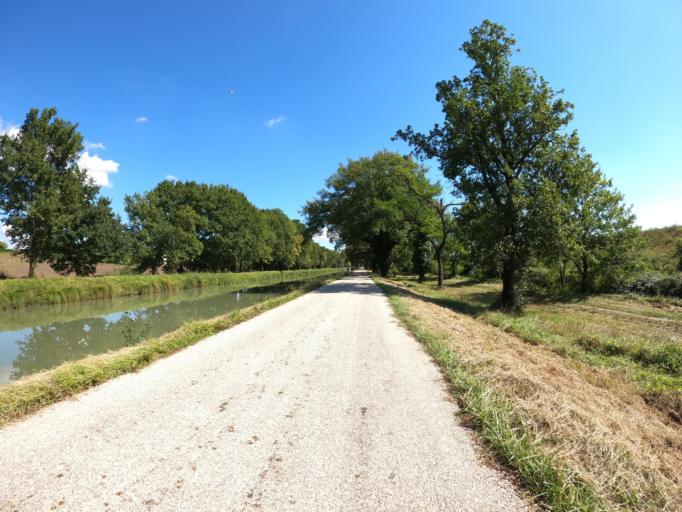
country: FR
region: Midi-Pyrenees
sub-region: Departement du Tarn-et-Garonne
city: Valence
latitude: 44.0999
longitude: 0.9177
